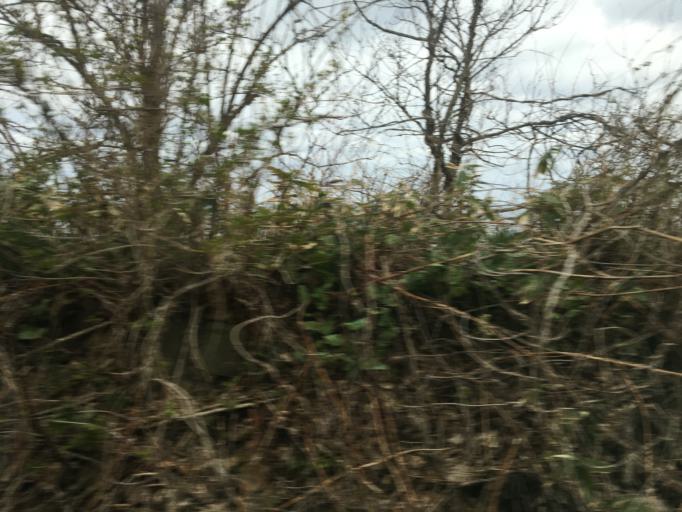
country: JP
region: Akita
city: Noshiromachi
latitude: 40.6178
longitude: 139.8706
